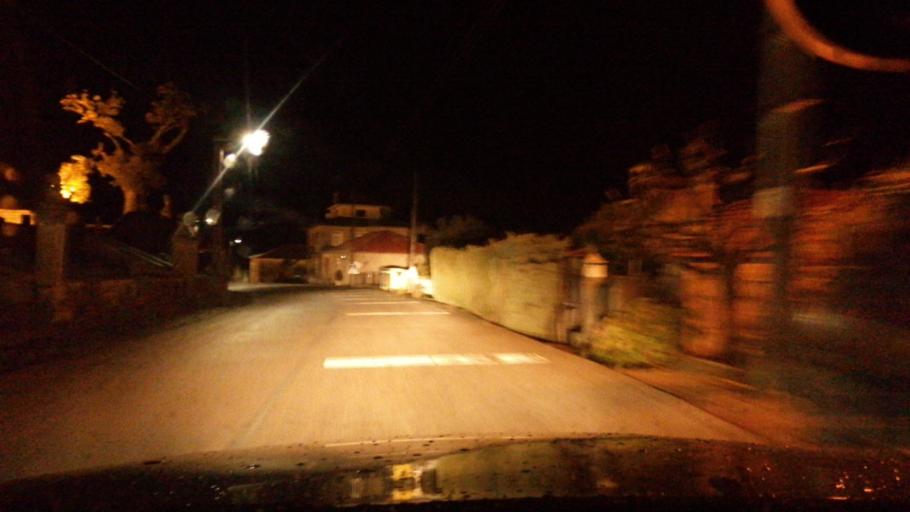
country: PT
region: Viseu
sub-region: Moimenta da Beira
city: Moimenta da Beira
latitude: 41.0399
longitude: -7.6399
